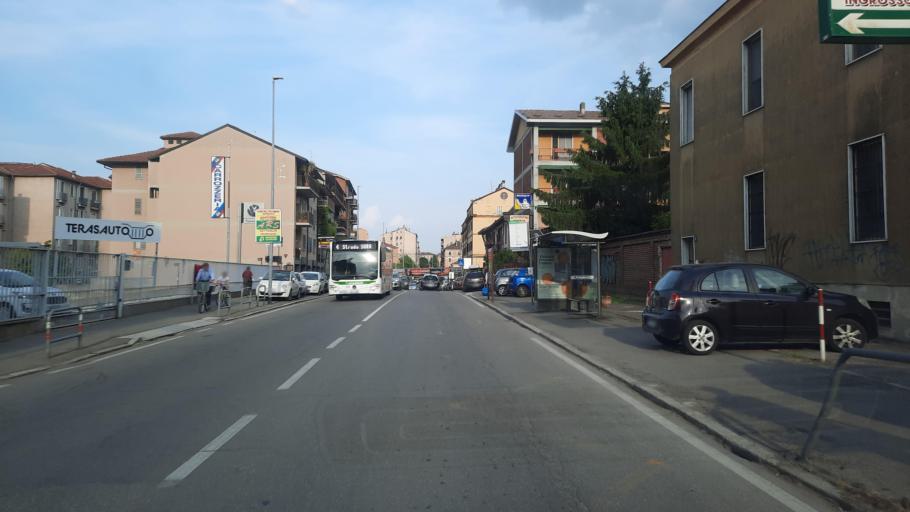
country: IT
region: Lombardy
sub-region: Provincia di Pavia
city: Pavia
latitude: 45.1881
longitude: 9.1393
